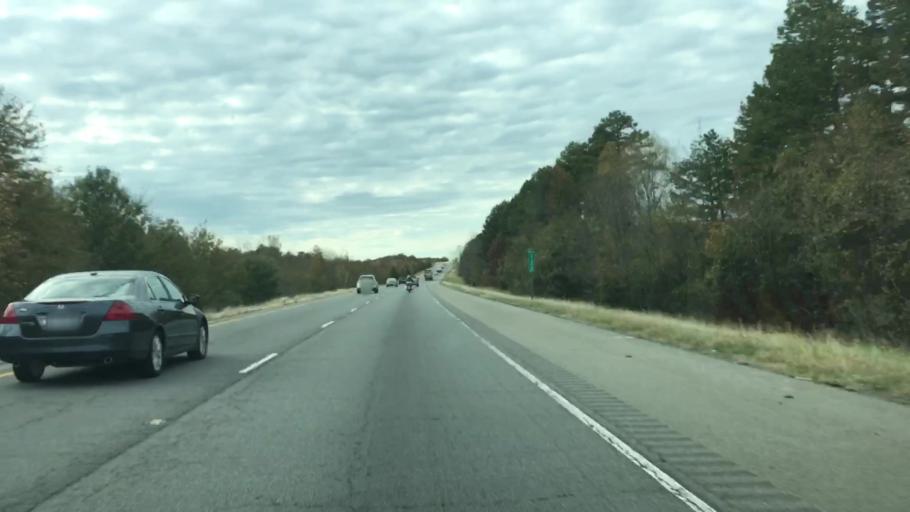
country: US
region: Arkansas
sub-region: Faulkner County
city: Conway
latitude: 35.1210
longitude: -92.4874
